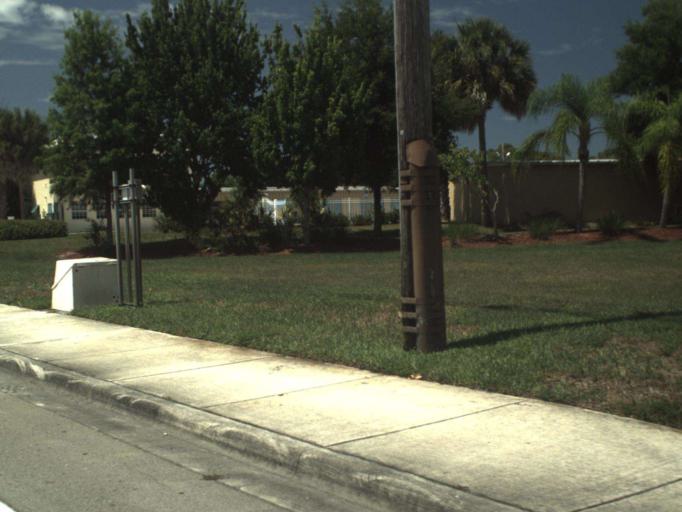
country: US
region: Florida
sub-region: Saint Lucie County
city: River Park
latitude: 27.3246
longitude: -80.3195
